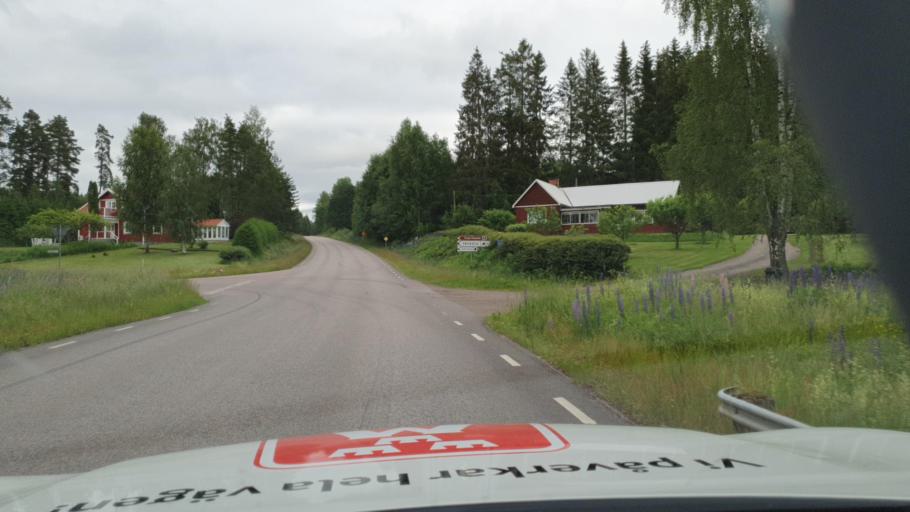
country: SE
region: Vaermland
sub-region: Kils Kommun
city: Kil
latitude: 59.5205
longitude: 13.3292
